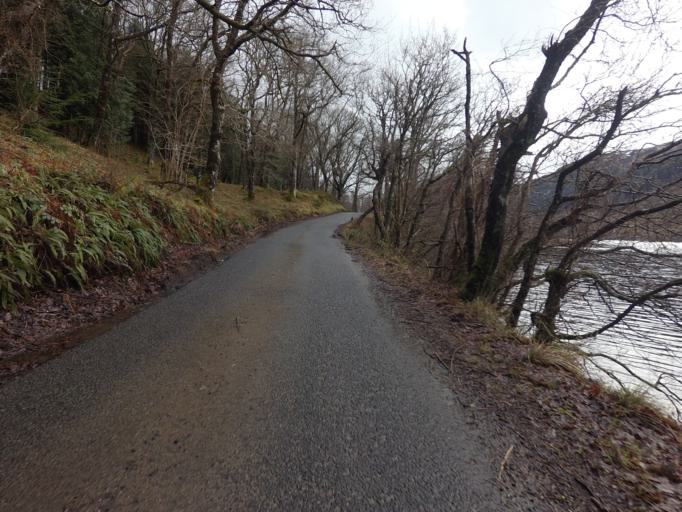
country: GB
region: Scotland
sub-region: West Dunbartonshire
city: Balloch
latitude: 56.2216
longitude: -4.5502
